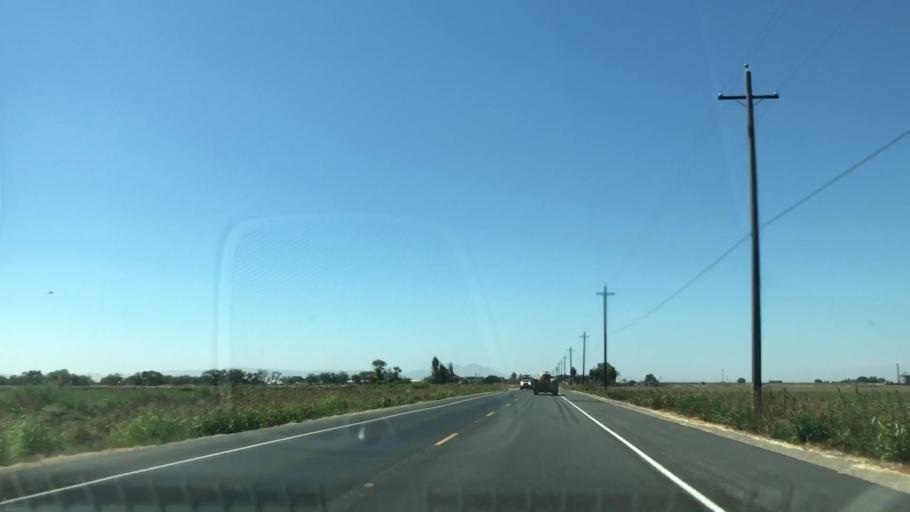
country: US
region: California
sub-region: San Joaquin County
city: Country Club
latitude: 37.9269
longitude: -121.4188
